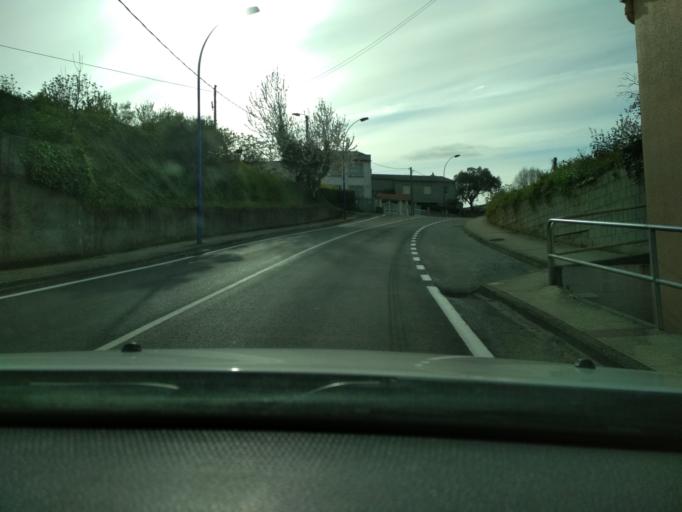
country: ES
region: Galicia
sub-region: Provincia da Coruna
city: Culleredo
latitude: 43.2870
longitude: -8.3875
